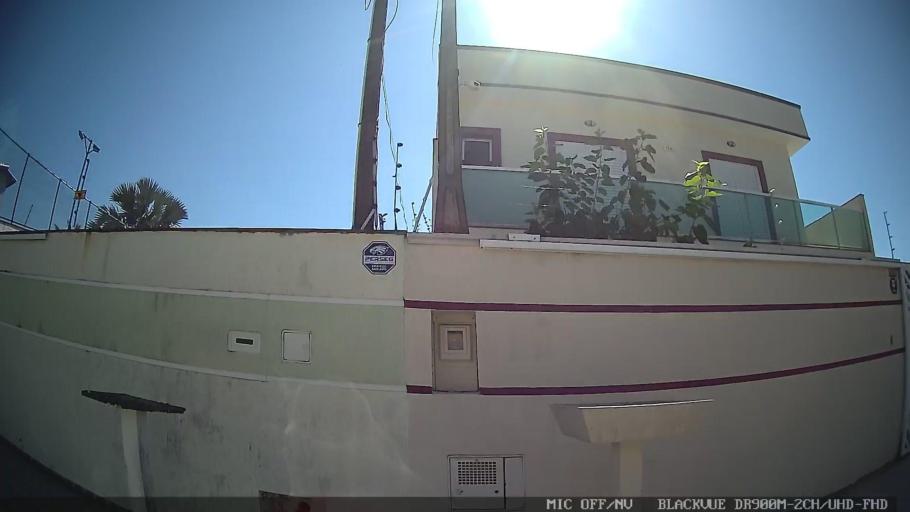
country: BR
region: Sao Paulo
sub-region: Peruibe
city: Peruibe
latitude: -24.2866
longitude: -46.9540
